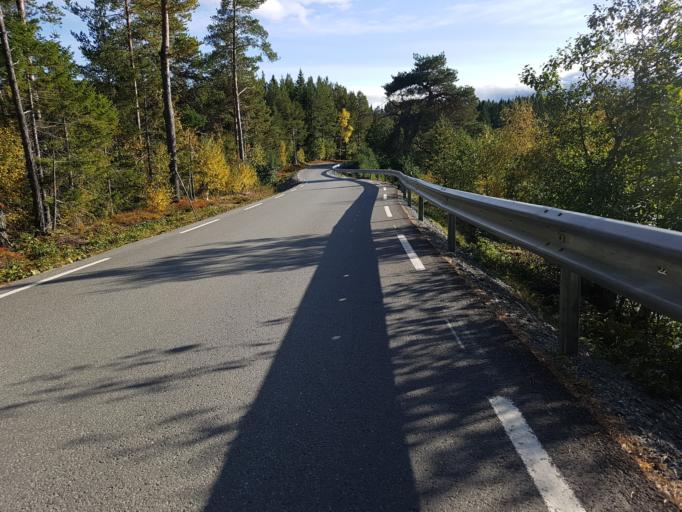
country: NO
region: Sor-Trondelag
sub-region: Malvik
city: Malvik
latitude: 63.3814
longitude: 10.5986
